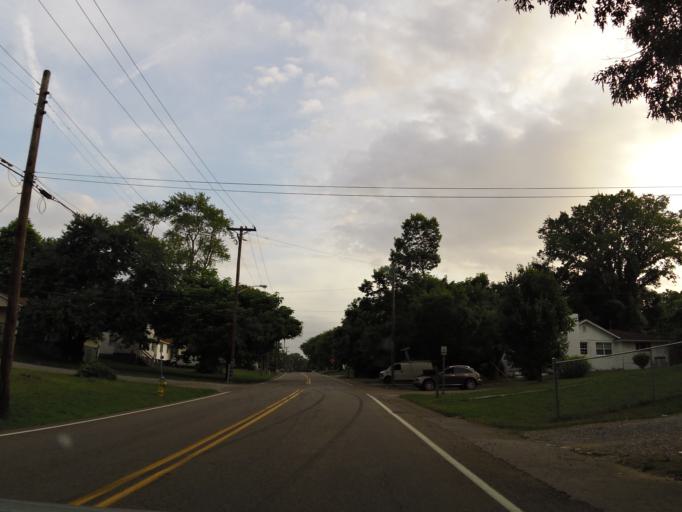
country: US
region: Tennessee
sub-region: Knox County
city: Knoxville
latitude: 35.9834
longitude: -83.8896
